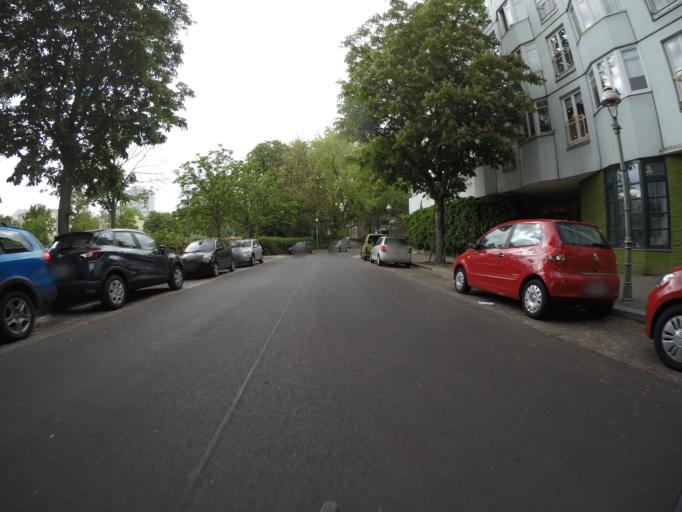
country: DE
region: Berlin
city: Hansaviertel
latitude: 52.5185
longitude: 13.3360
